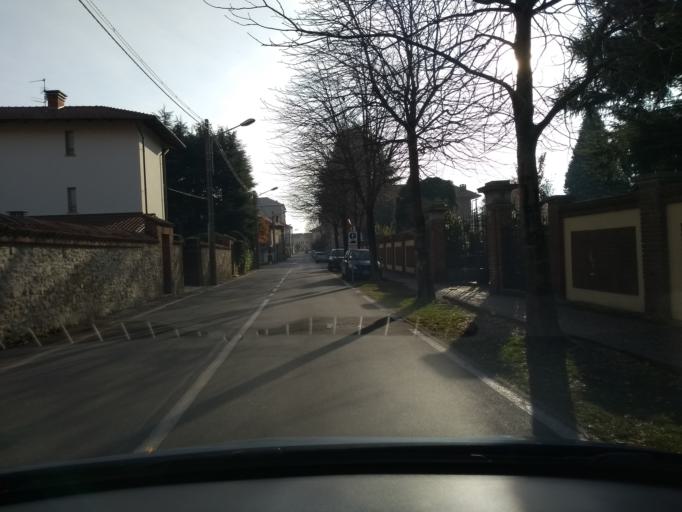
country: IT
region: Piedmont
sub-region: Provincia di Torino
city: Balangero
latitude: 45.2688
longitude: 7.5199
